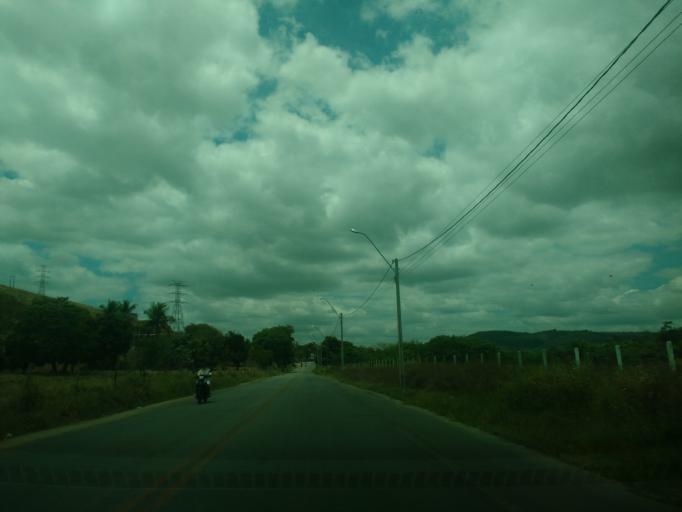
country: BR
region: Alagoas
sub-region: Uniao Dos Palmares
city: Uniao dos Palmares
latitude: -9.1488
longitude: -36.0368
